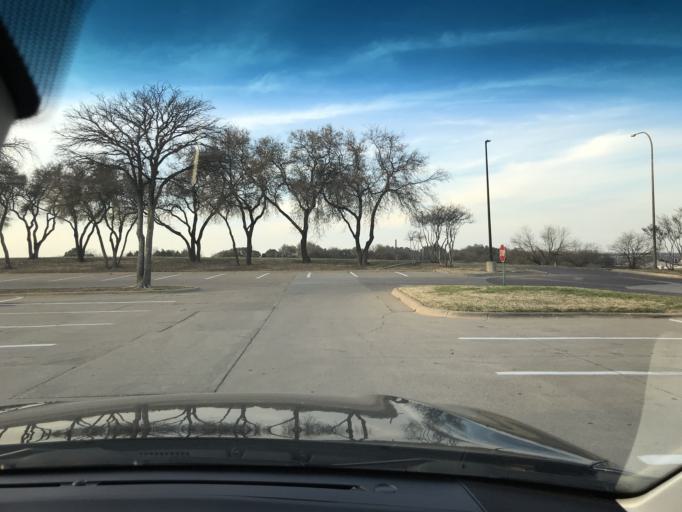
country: US
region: Texas
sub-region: Tarrant County
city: Benbrook
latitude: 32.6822
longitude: -97.4167
